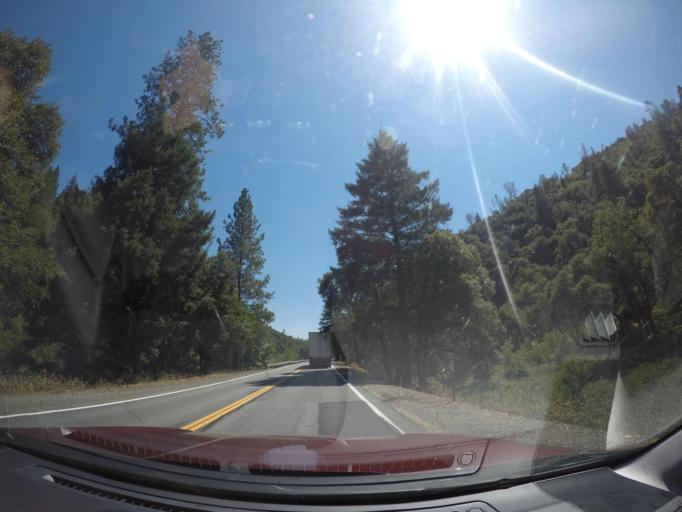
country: US
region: California
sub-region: Shasta County
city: Bella Vista
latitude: 40.7395
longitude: -122.0720
